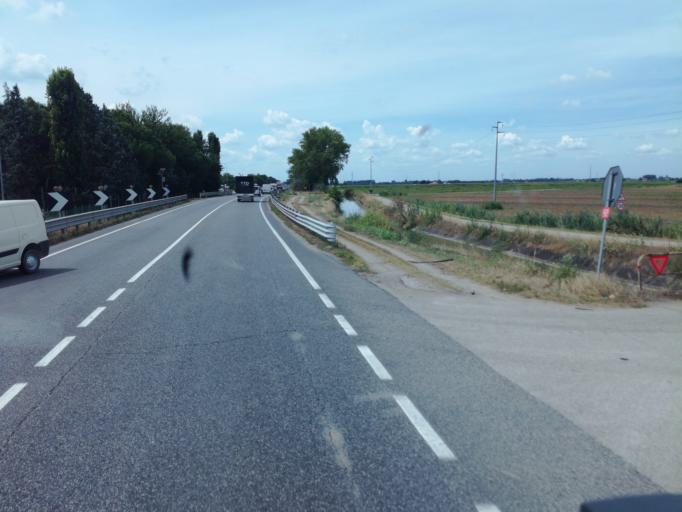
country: IT
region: Emilia-Romagna
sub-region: Provincia di Ferrara
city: Bosco Mesola
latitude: 44.8951
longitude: 12.2208
